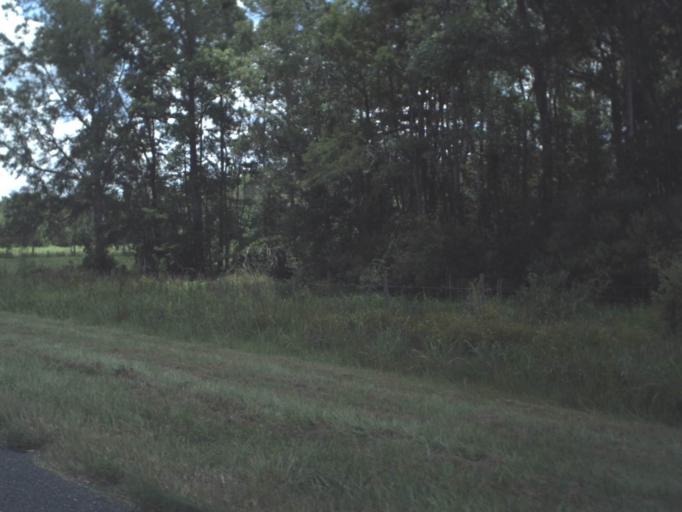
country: US
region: Florida
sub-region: Taylor County
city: Steinhatchee
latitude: 29.9088
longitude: -83.4284
